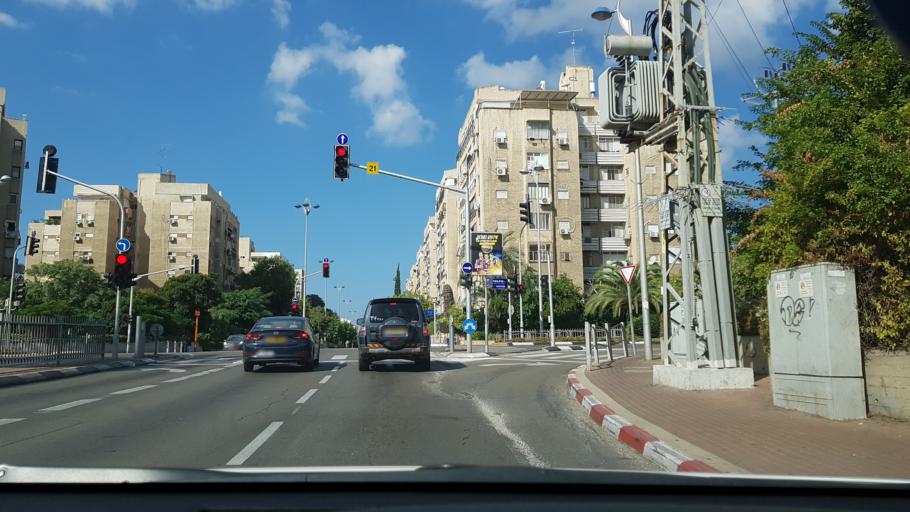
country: IL
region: Tel Aviv
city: Holon
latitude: 32.0100
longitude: 34.7927
